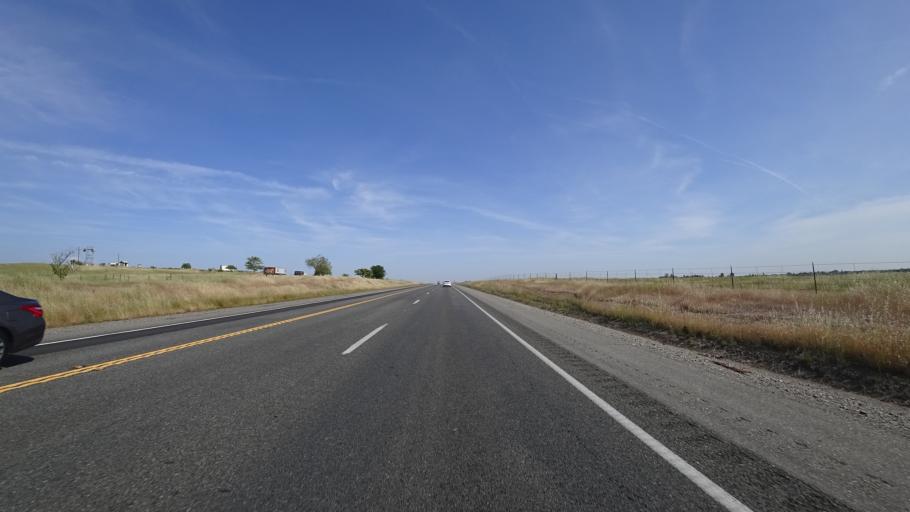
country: US
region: California
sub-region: Tehama County
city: Los Molinos
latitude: 39.9293
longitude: -122.0302
